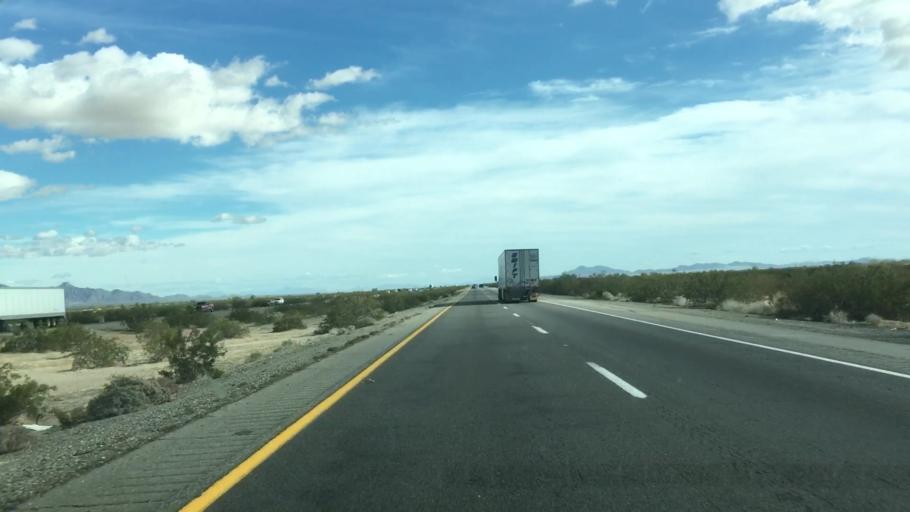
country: US
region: California
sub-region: Riverside County
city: Mesa Verde
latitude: 33.6279
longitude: -115.0639
